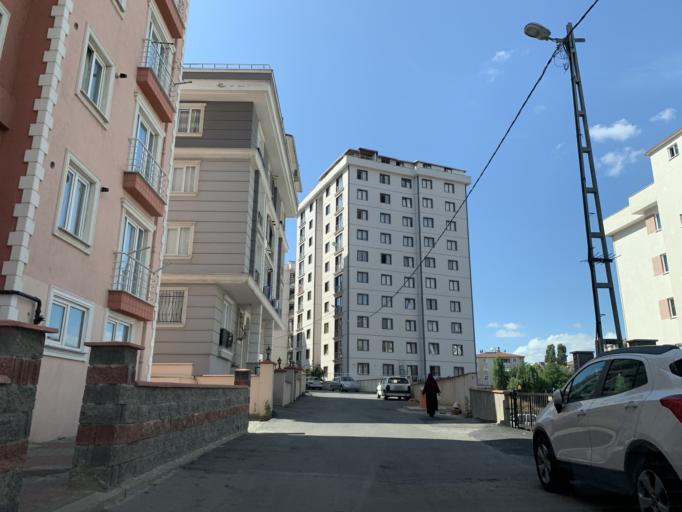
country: TR
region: Istanbul
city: Pendik
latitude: 40.8911
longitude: 29.2737
